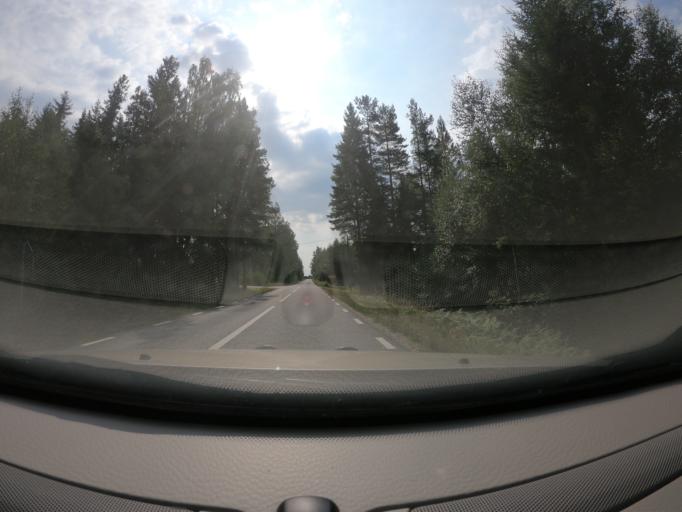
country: SE
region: Kronoberg
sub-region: Vaxjo Kommun
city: Braas
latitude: 57.1438
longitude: 14.9607
